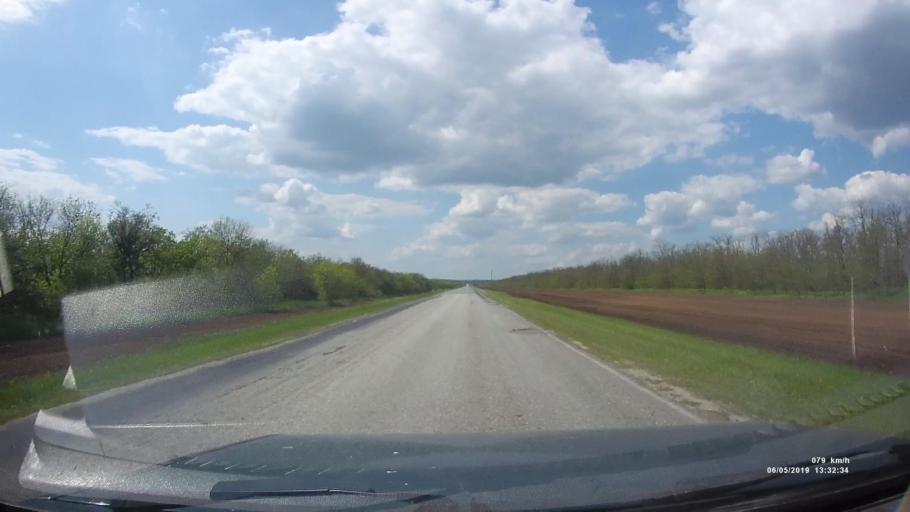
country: RU
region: Rostov
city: Ust'-Donetskiy
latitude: 47.6847
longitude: 40.7933
